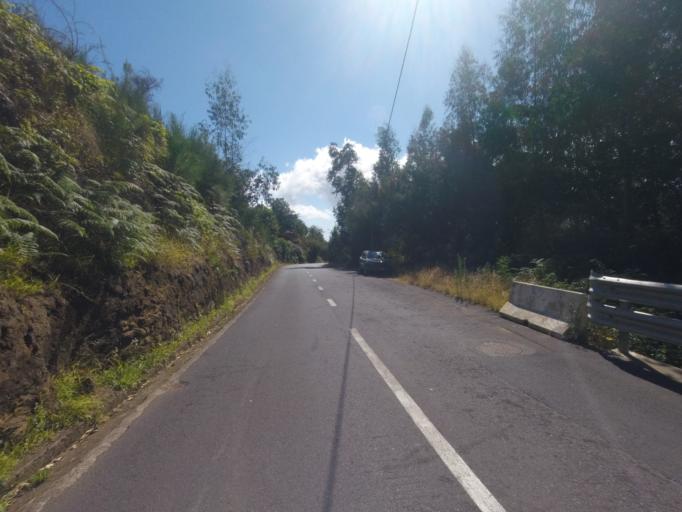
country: PT
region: Madeira
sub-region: Ribeira Brava
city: Campanario
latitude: 32.6935
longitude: -17.0310
